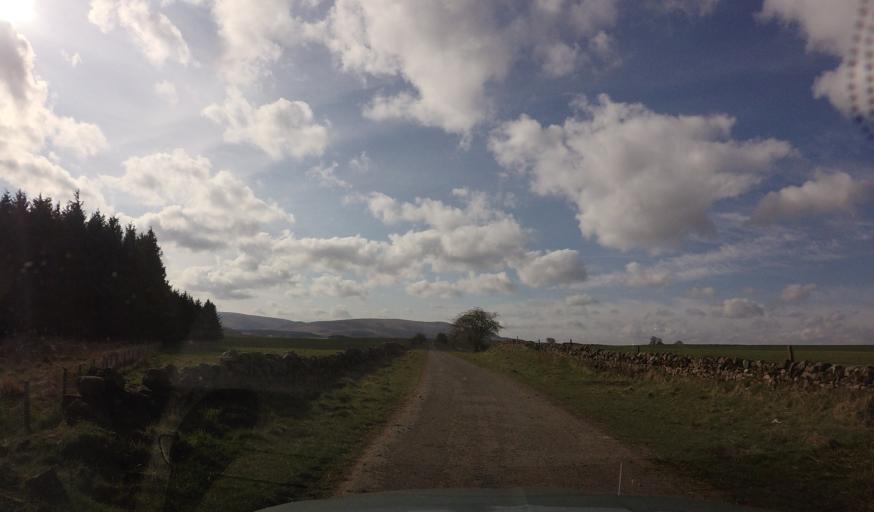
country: GB
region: Scotland
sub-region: Midlothian
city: Penicuik
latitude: 55.7968
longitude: -3.1676
